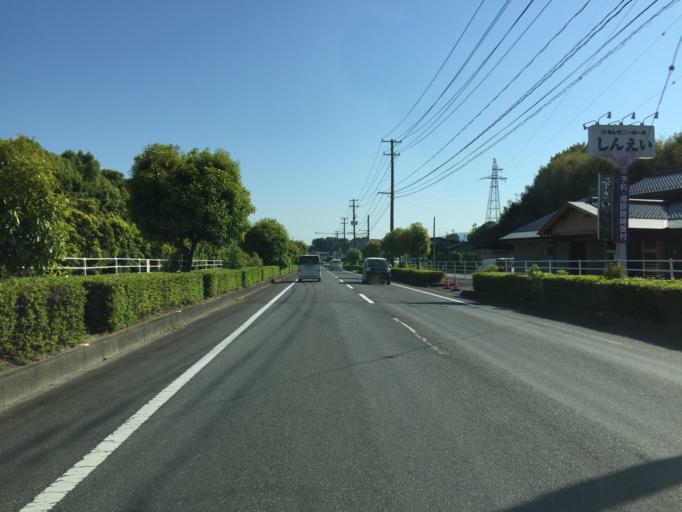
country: JP
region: Ibaraki
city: Kitaibaraki
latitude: 36.9027
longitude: 140.7695
